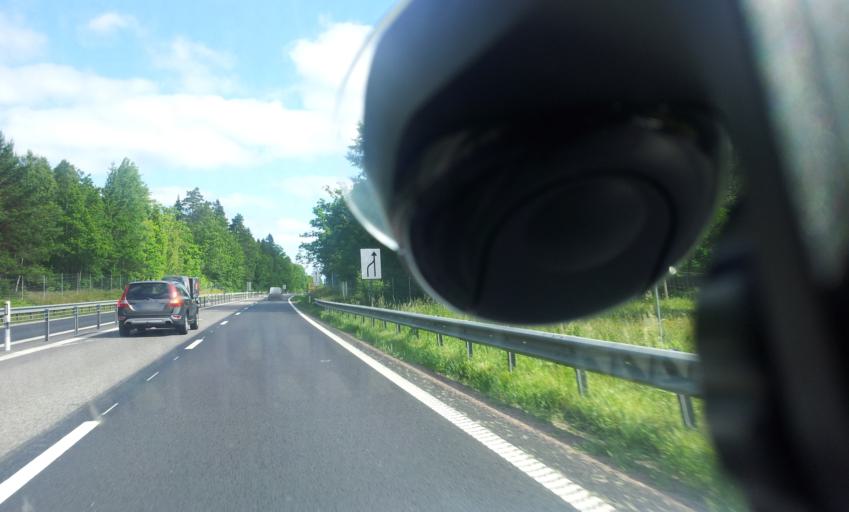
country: SE
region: Kalmar
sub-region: Monsteras Kommun
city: Timmernabben
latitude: 56.9034
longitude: 16.3792
